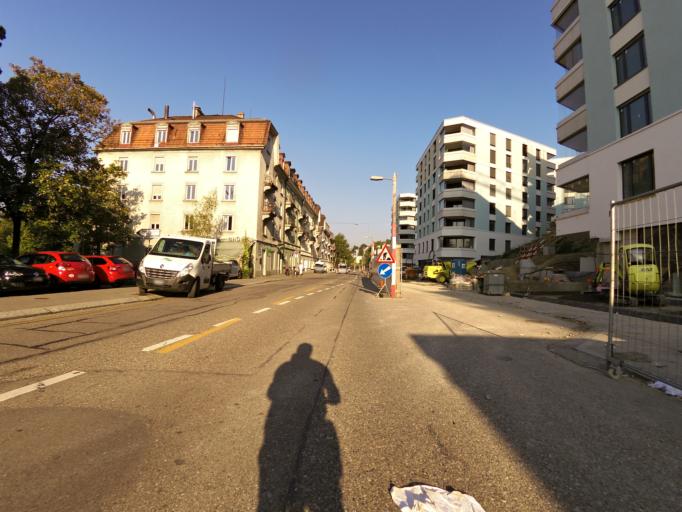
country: CH
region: Zurich
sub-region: Bezirk Zuerich
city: Zuerich (Kreis 10) / Wipkingen
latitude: 47.3931
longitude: 8.5216
